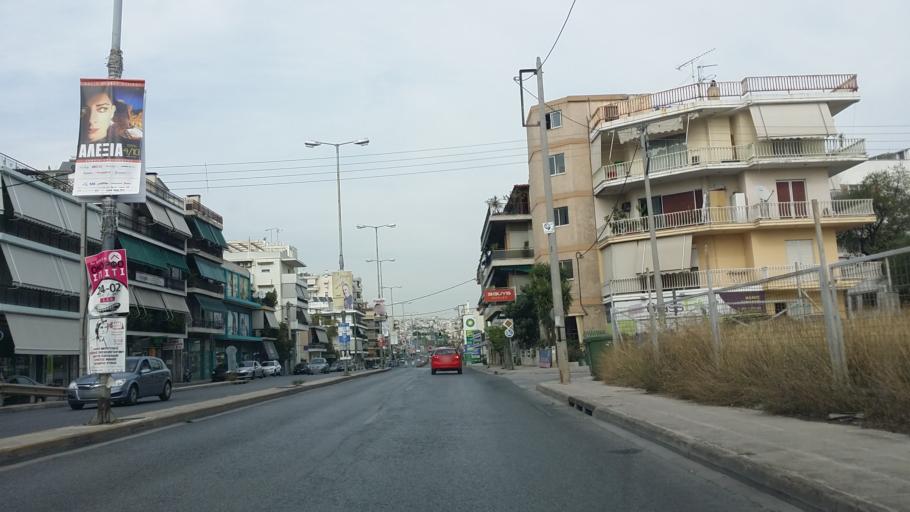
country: GR
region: Attica
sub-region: Nomarchia Athinas
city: Filothei
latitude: 38.0355
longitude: 23.7723
